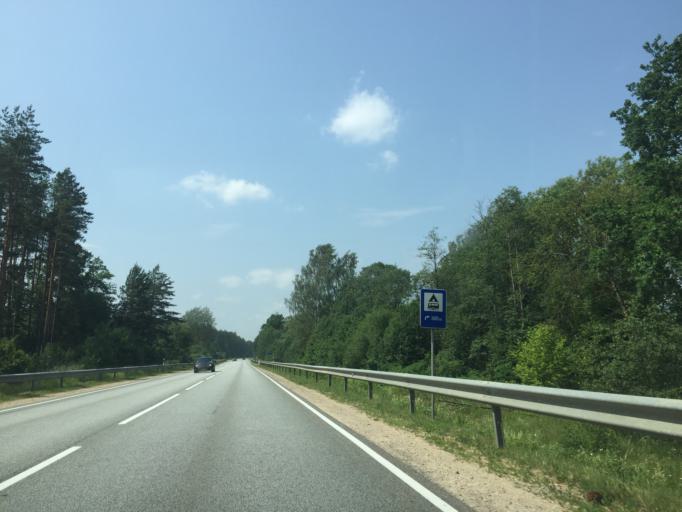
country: LV
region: Kekava
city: Kekava
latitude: 56.8098
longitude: 24.2075
